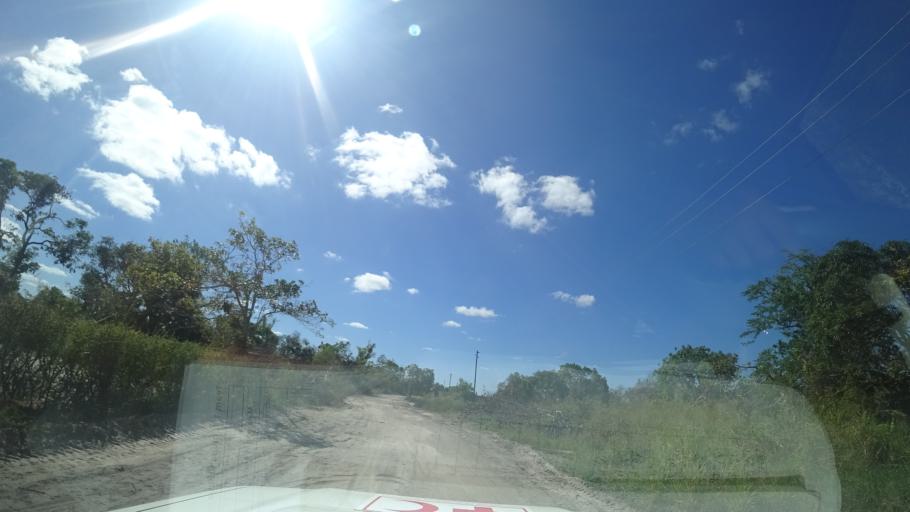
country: MZ
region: Sofala
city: Dondo
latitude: -19.5041
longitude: 34.6118
